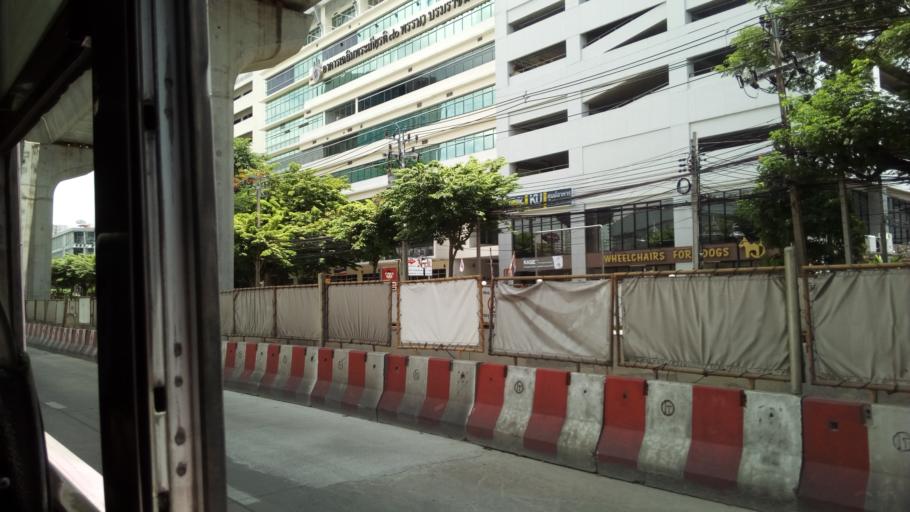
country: TH
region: Bangkok
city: Chatuchak
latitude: 13.8447
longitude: 100.5786
